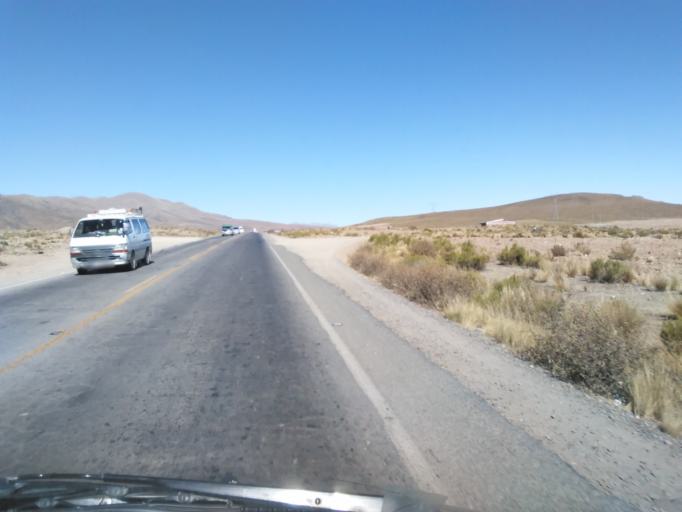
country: BO
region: Oruro
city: Machacamarca
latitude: -18.0415
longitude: -67.0151
